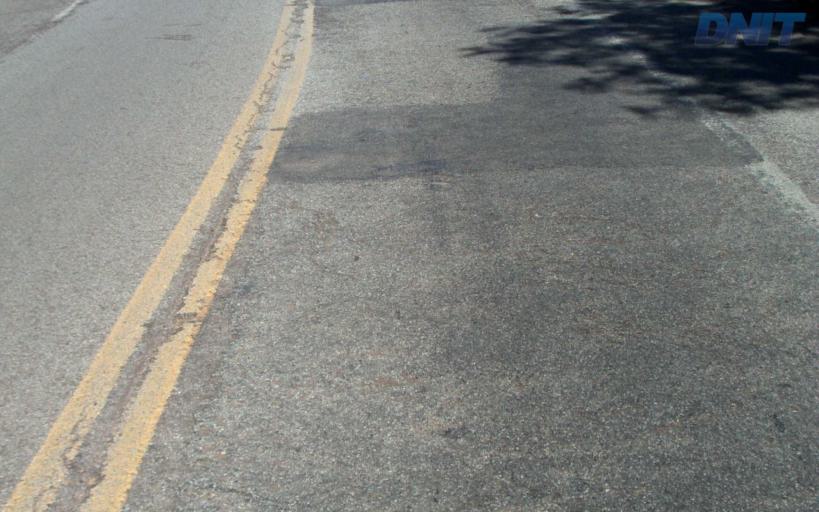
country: BR
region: Minas Gerais
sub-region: Caete
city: Caete
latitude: -19.7235
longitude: -43.5795
